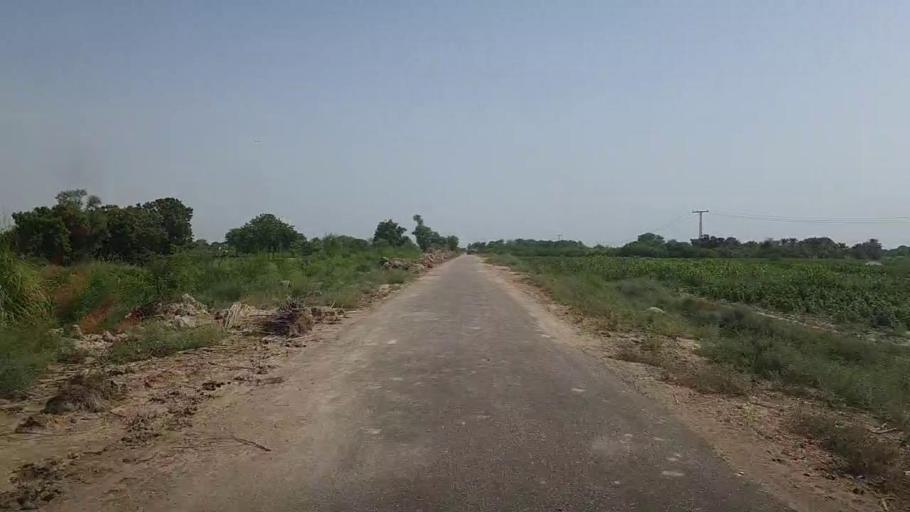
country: PK
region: Sindh
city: Pad Idan
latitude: 26.8233
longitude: 68.3279
